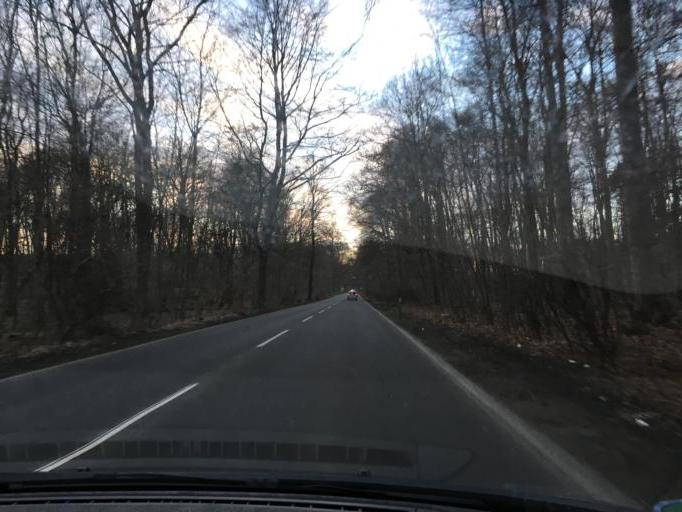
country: DE
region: North Rhine-Westphalia
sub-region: Regierungsbezirk Koln
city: Neustadt/Sued
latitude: 50.9077
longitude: 6.9109
